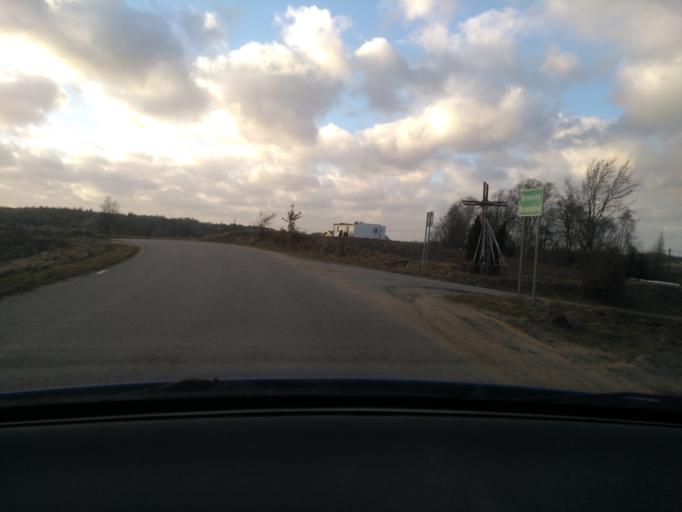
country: PL
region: Pomeranian Voivodeship
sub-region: Powiat kartuski
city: Kartuzy
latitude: 54.3696
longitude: 18.2200
